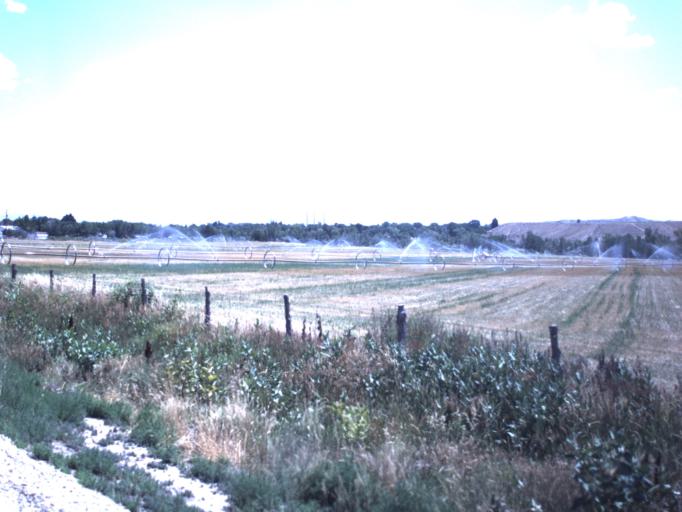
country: US
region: Utah
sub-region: Emery County
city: Orangeville
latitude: 39.2414
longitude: -111.0615
